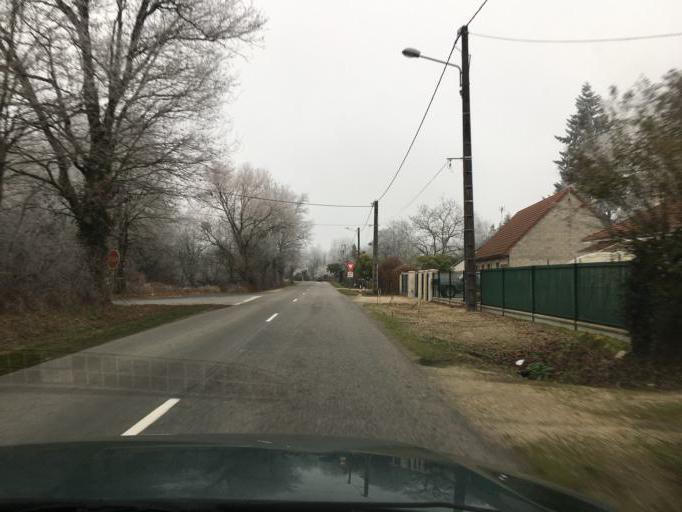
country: FR
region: Centre
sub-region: Departement du Loiret
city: Ligny-le-Ribault
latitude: 47.6802
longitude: 1.7826
